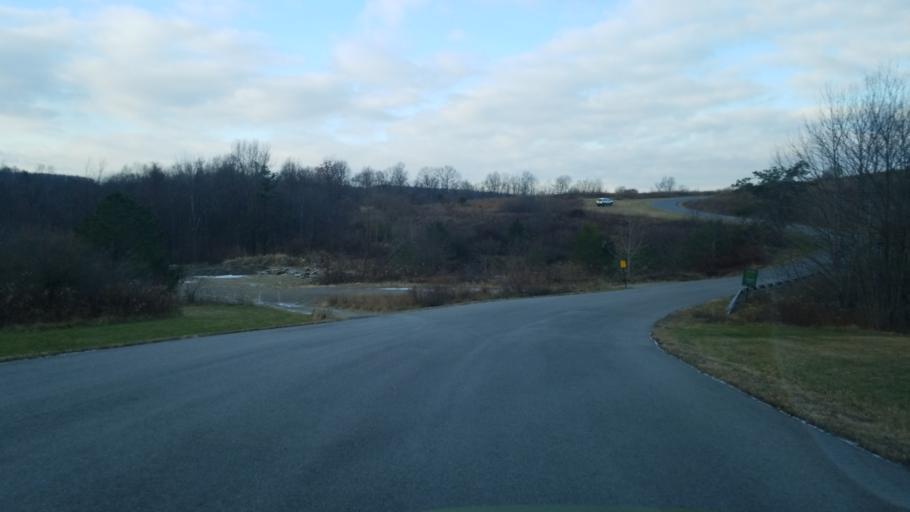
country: US
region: Pennsylvania
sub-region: Clearfield County
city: Clearfield
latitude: 41.0080
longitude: -78.4196
